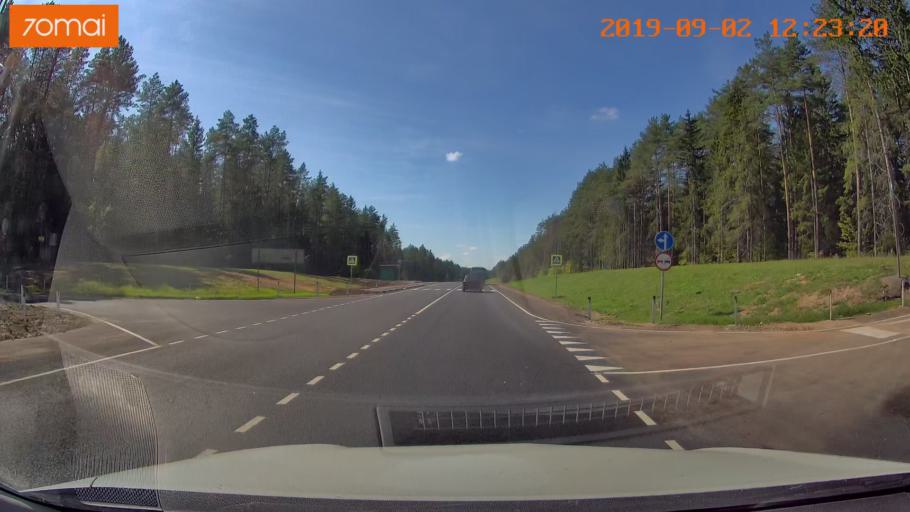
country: RU
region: Smolensk
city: Shumyachi
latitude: 53.8751
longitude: 32.6215
